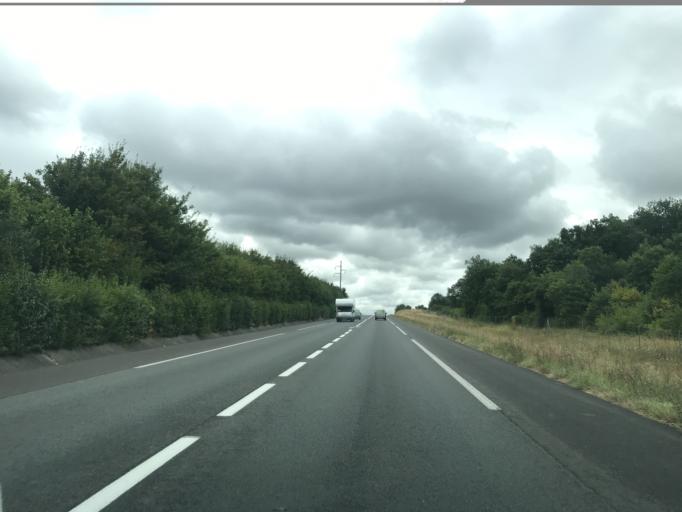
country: FR
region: Poitou-Charentes
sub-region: Departement de la Charente
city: Puymoyen
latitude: 45.6259
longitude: 0.1704
